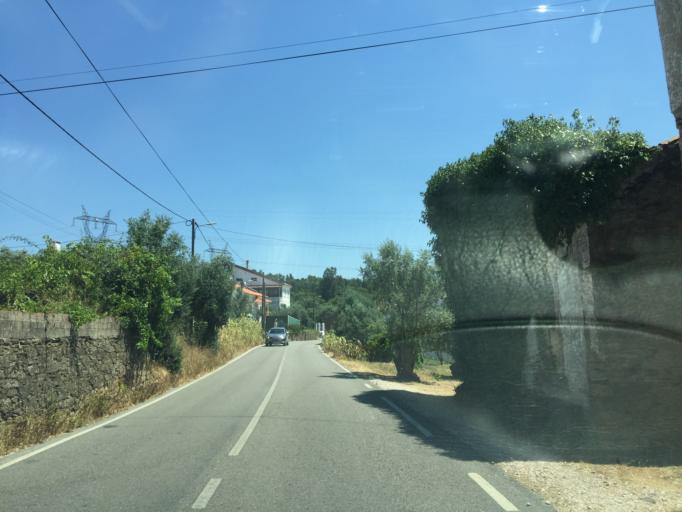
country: PT
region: Santarem
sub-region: Tomar
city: Tomar
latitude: 39.5965
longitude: -8.3218
